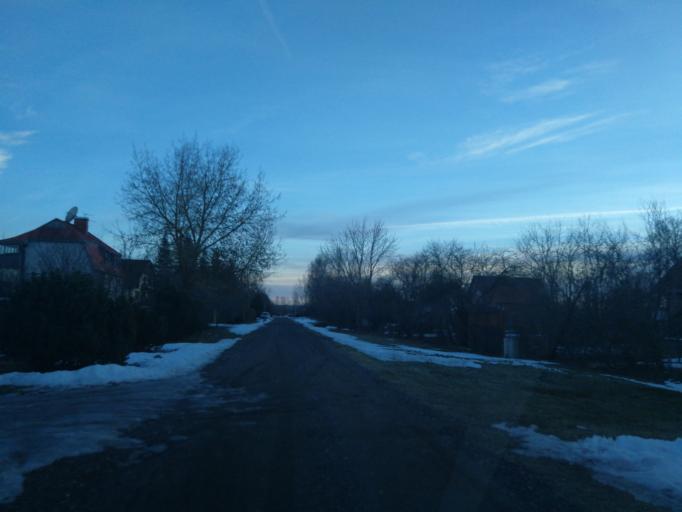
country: LV
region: Adazi
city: Adazi
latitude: 57.0915
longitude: 24.3156
